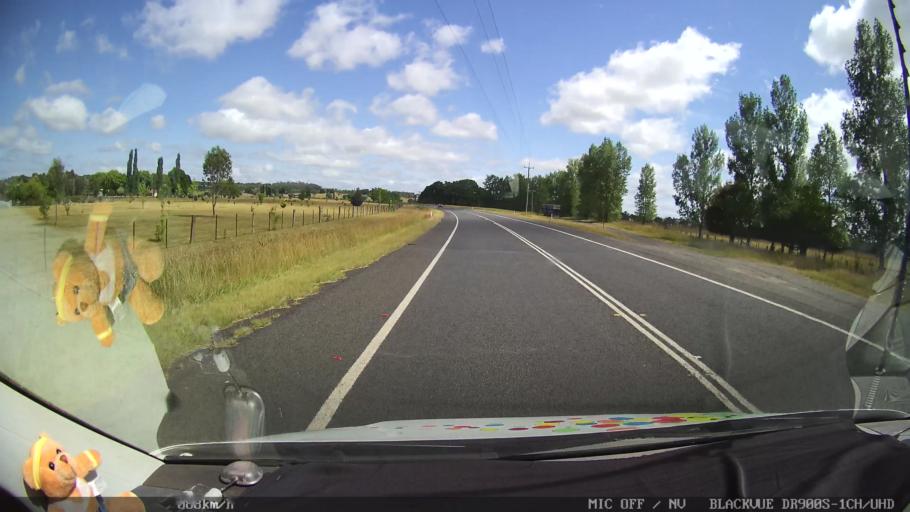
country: AU
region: New South Wales
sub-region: Glen Innes Severn
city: Glen Innes
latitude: -29.8131
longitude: 151.7413
